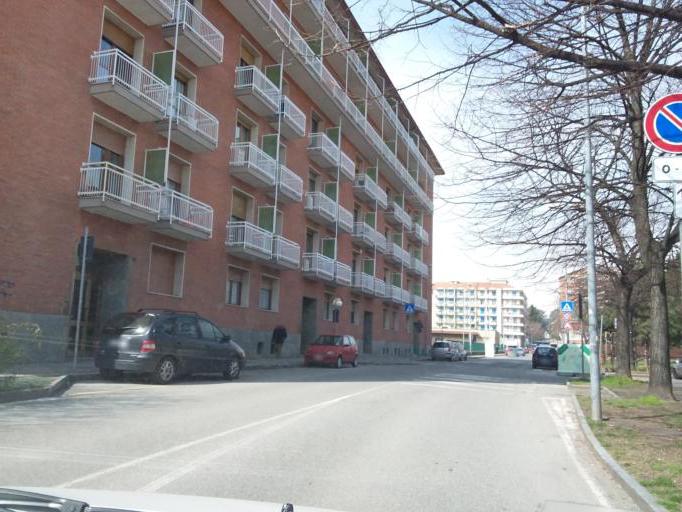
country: IT
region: Piedmont
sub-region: Provincia di Torino
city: Rivoli
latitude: 45.0731
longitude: 7.5236
